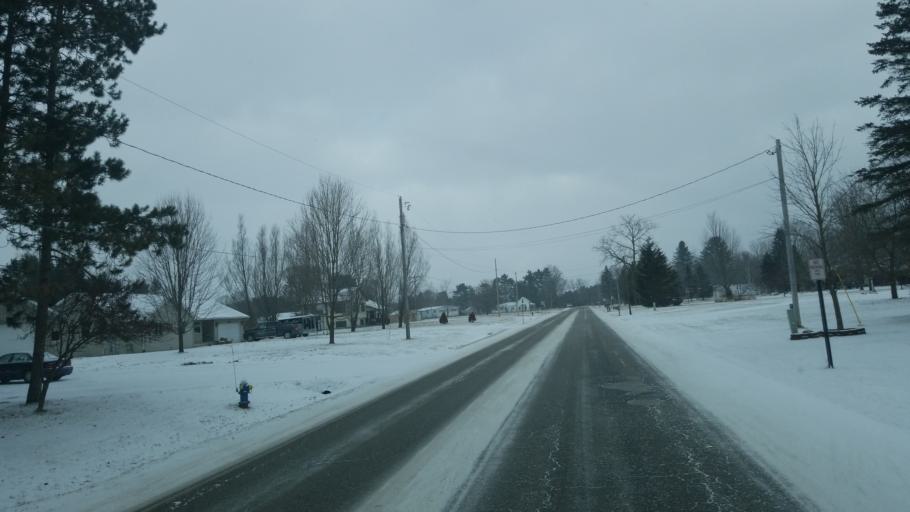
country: US
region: Michigan
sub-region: Osceola County
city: Evart
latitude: 43.9136
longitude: -85.2549
